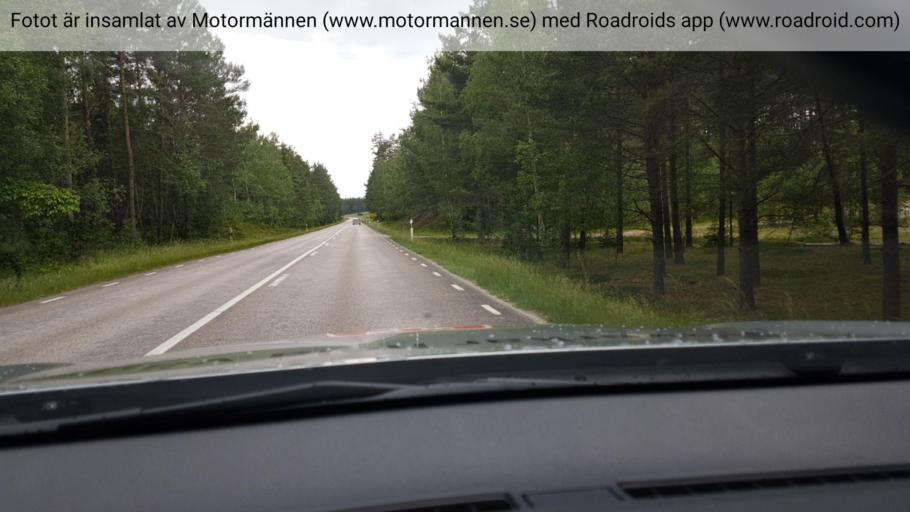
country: SE
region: Vaestra Goetaland
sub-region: Hjo Kommun
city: Hjo
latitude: 58.1952
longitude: 14.2062
